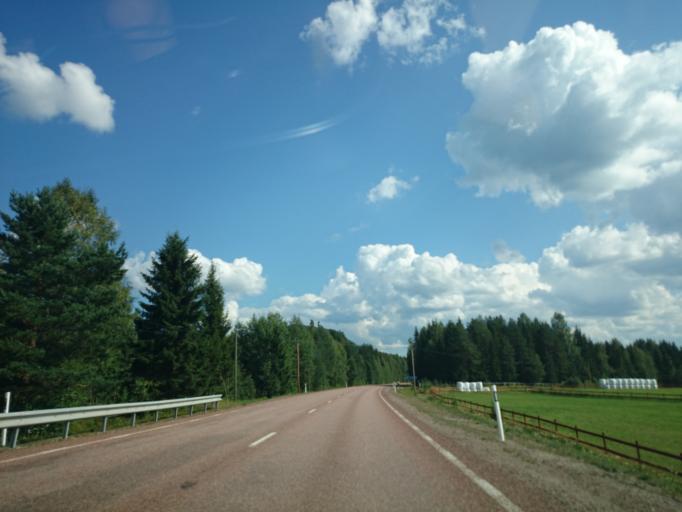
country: SE
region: Gaevleborg
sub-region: Ljusdals Kommun
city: Jaervsoe
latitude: 61.8044
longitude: 16.2921
